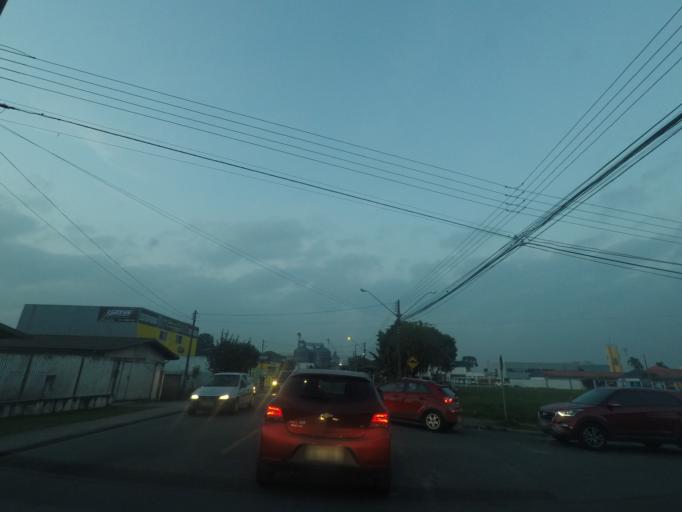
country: BR
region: Parana
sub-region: Pinhais
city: Pinhais
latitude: -25.4497
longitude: -49.1891
